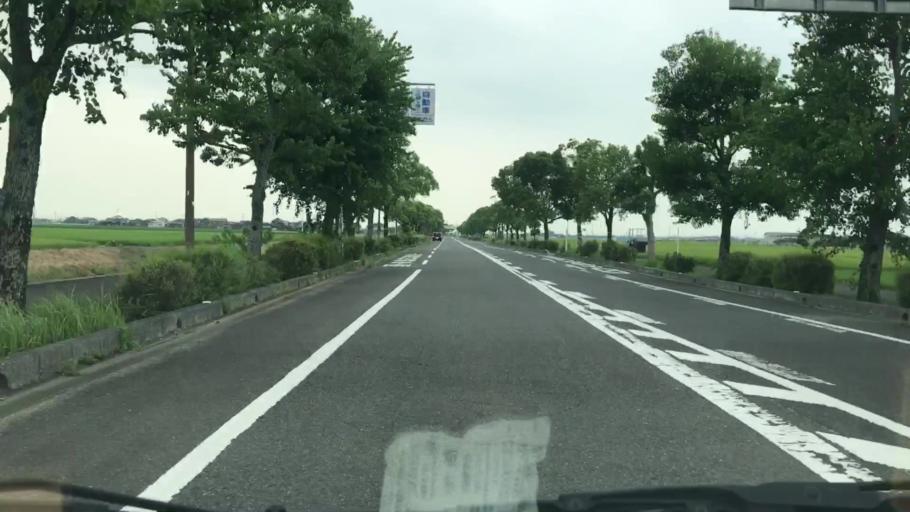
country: JP
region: Saga Prefecture
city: Saga-shi
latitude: 33.2126
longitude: 130.3046
